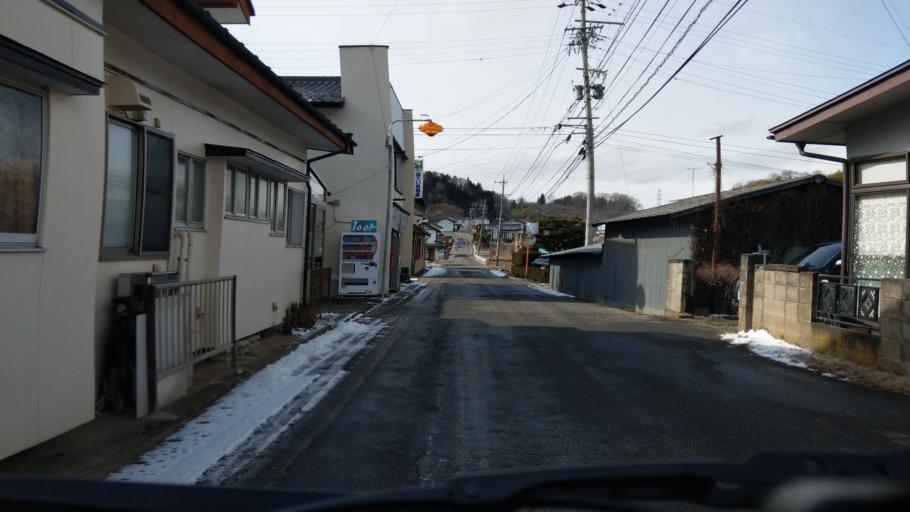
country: JP
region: Nagano
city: Kamimaruko
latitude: 36.2699
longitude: 138.3346
